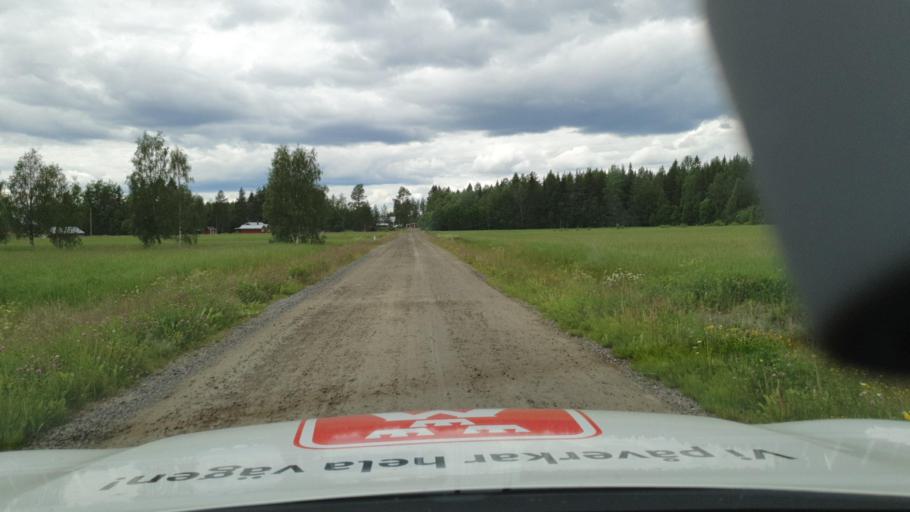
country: SE
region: Vaesterbotten
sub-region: Bjurholms Kommun
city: Bjurholm
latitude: 63.7940
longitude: 19.0944
